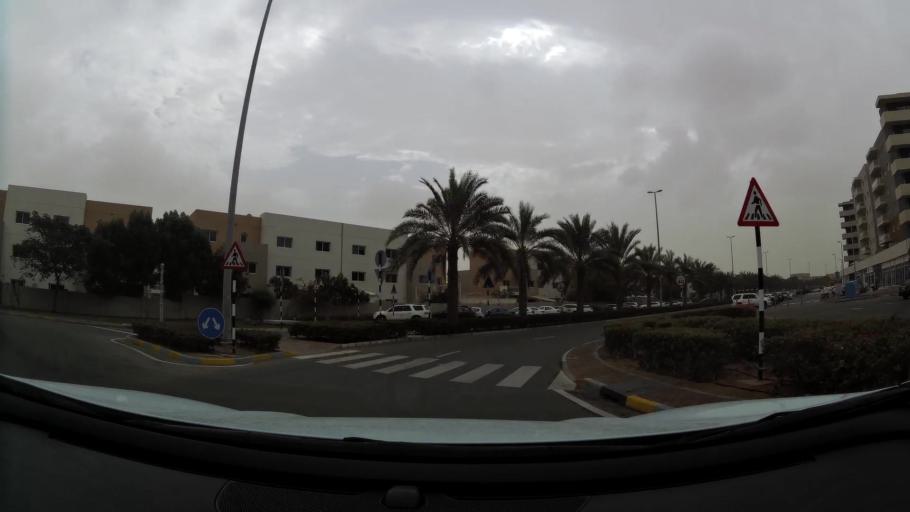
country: AE
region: Abu Dhabi
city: Abu Dhabi
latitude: 24.4582
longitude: 54.6741
